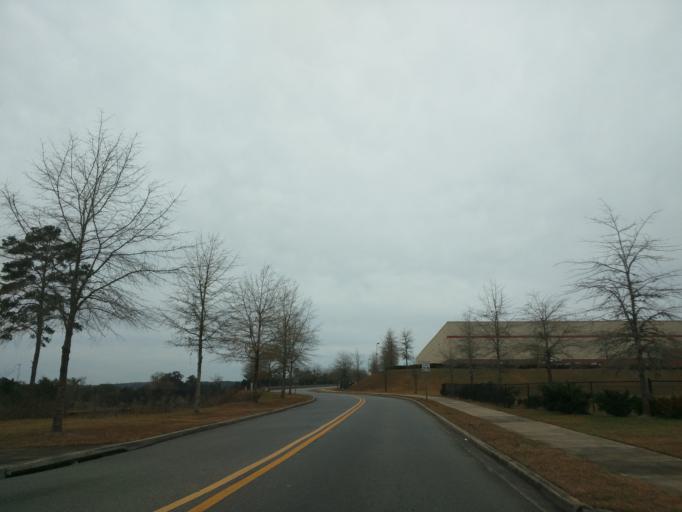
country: US
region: Florida
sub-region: Leon County
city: Tallahassee
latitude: 30.4599
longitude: -84.2103
